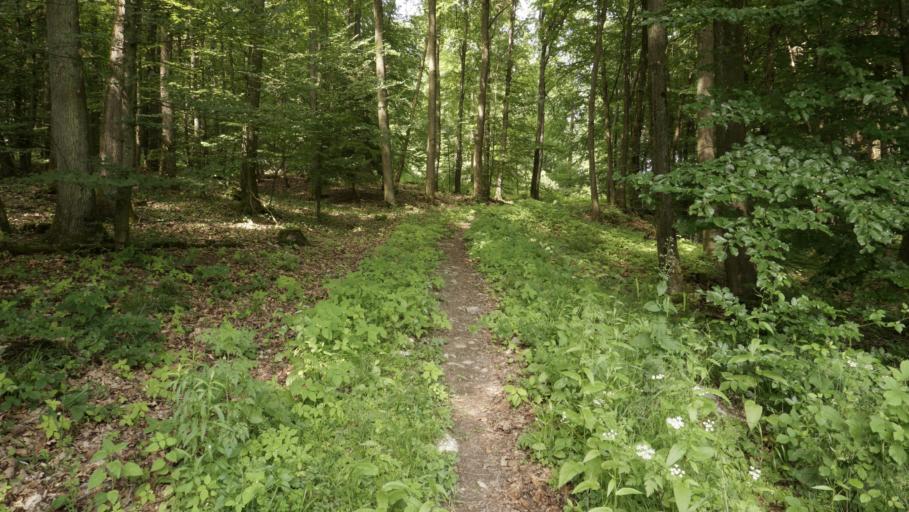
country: DE
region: Baden-Wuerttemberg
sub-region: Karlsruhe Region
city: Mosbach
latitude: 49.3403
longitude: 9.1963
